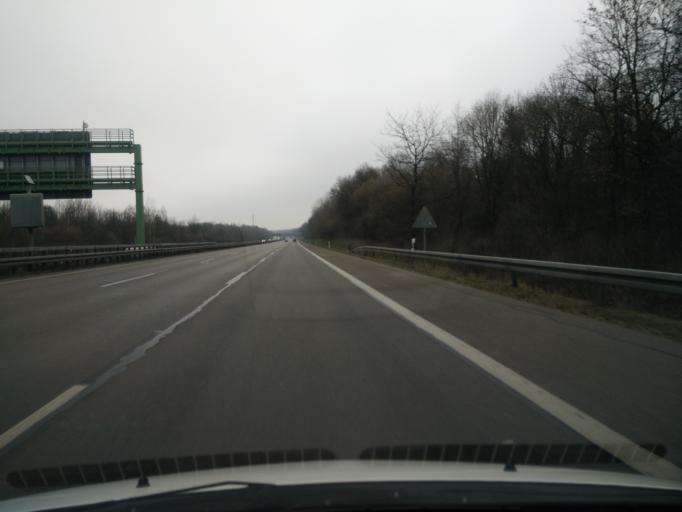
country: DE
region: Bavaria
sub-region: Upper Bavaria
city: Oberschleissheim
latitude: 48.2266
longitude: 11.5519
